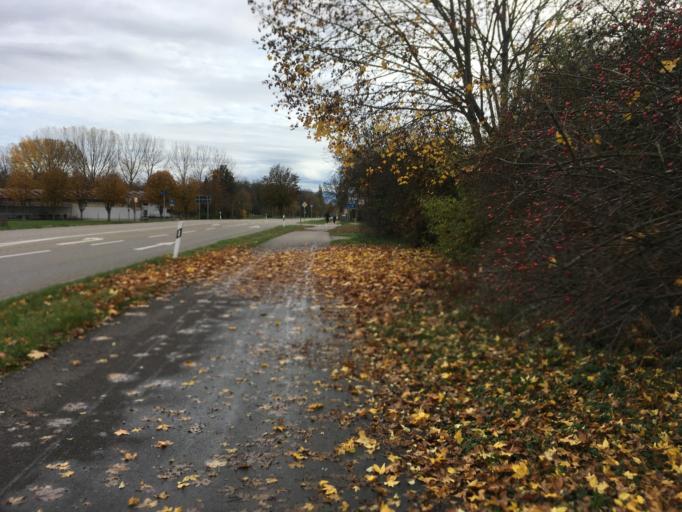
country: DE
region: Baden-Wuerttemberg
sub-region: Freiburg Region
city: Ihringen
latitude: 48.0321
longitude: 7.6578
